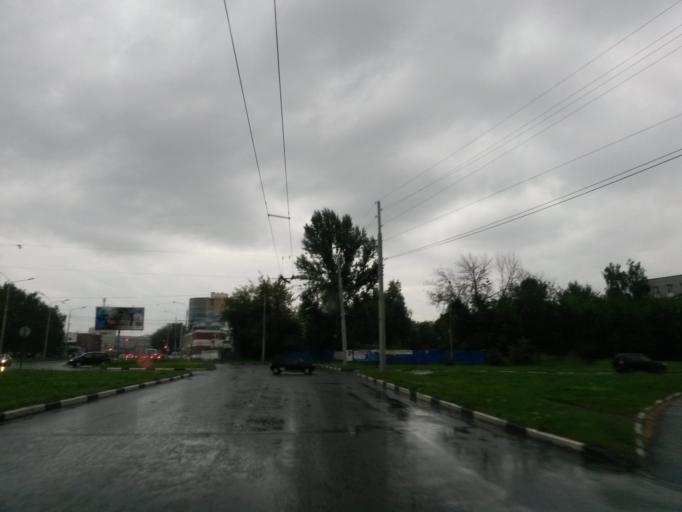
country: RU
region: Jaroslavl
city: Yaroslavl
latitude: 57.6452
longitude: 39.8810
